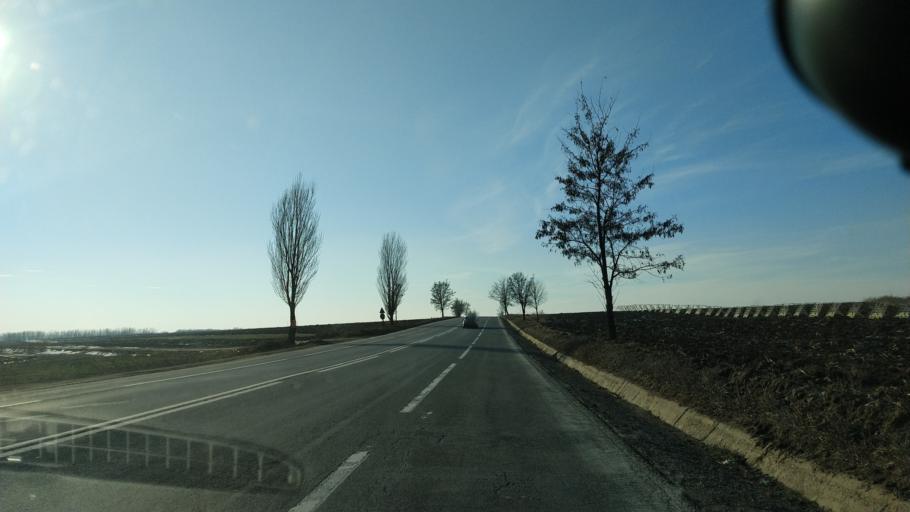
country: RO
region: Iasi
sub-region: Comuna Butea
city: Butea
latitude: 47.0910
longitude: 26.9172
